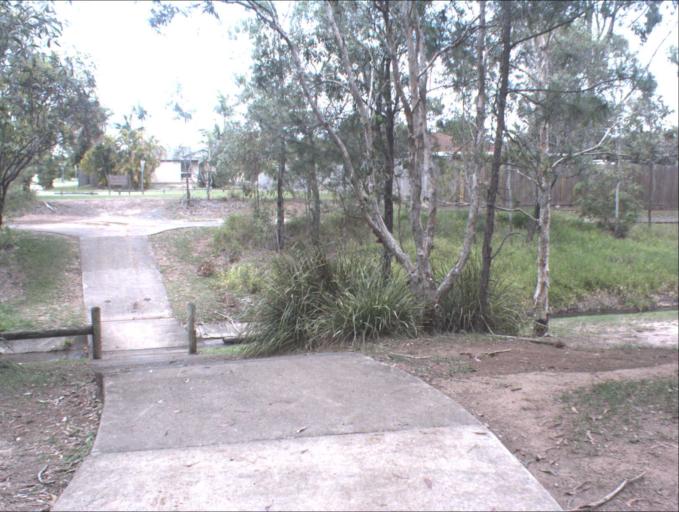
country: AU
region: Queensland
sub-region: Logan
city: Waterford West
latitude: -27.6874
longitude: 153.1284
